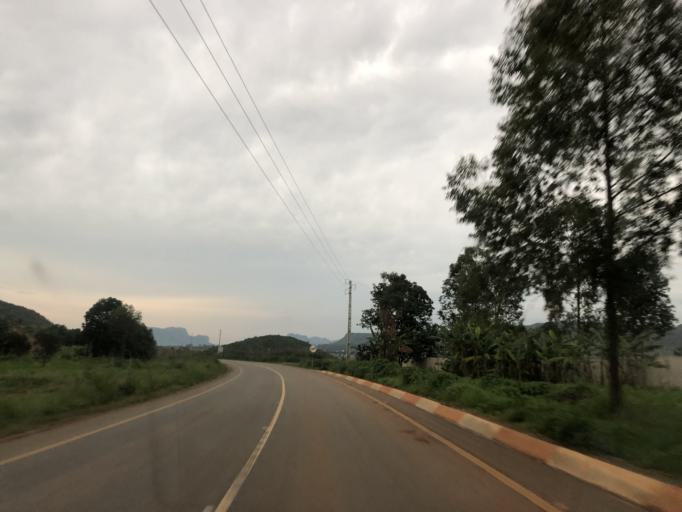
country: AO
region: Cuanza Sul
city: Uacu Cungo
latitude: -11.3247
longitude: 15.0896
